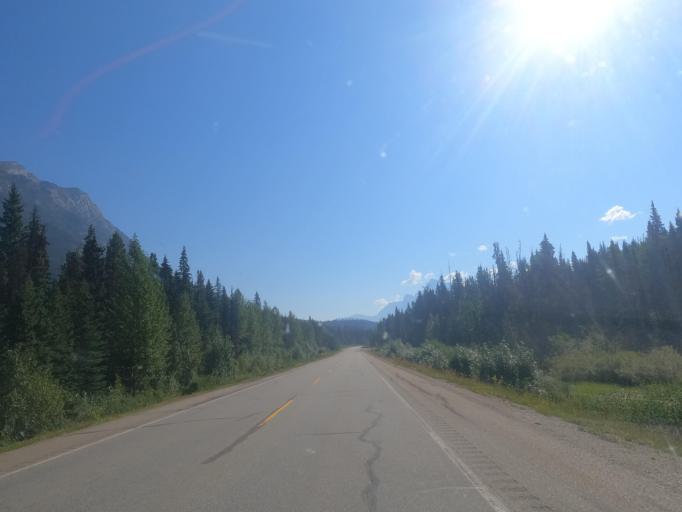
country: CA
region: Alberta
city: Jasper Park Lodge
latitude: 52.8631
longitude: -118.6539
